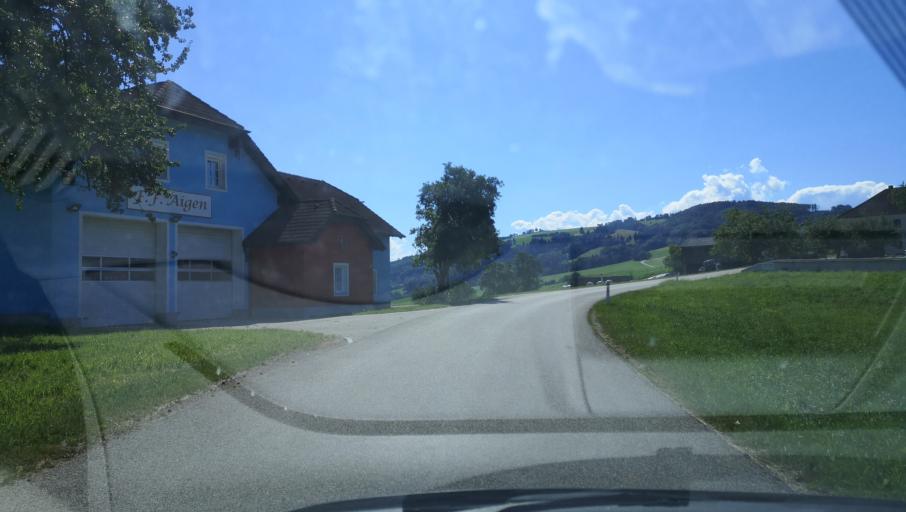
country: AT
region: Lower Austria
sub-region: Politischer Bezirk Amstetten
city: Euratsfeld
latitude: 48.0484
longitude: 14.9156
